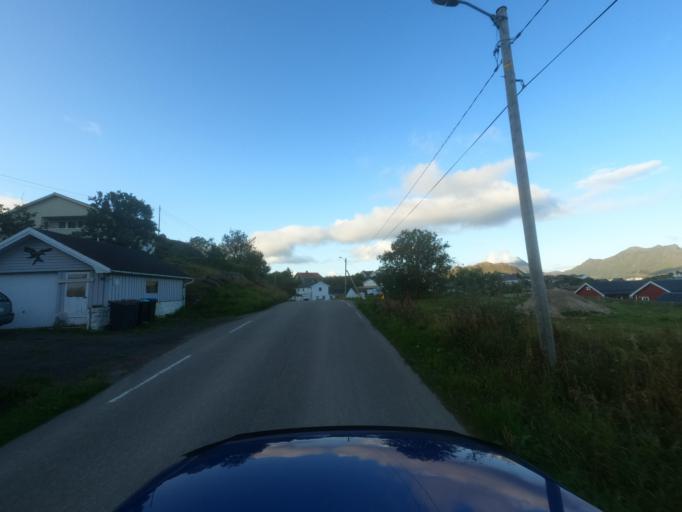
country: NO
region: Nordland
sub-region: Vestvagoy
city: Gravdal
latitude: 68.0769
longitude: 13.5303
